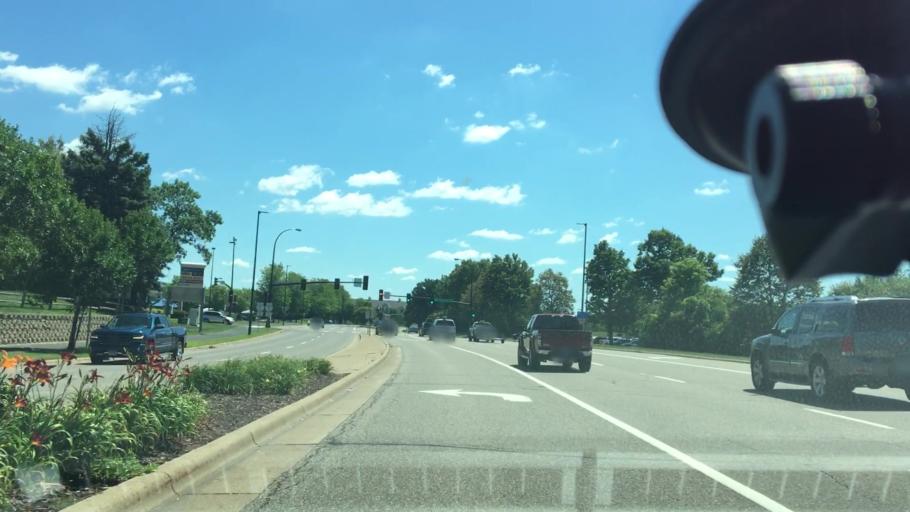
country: US
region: Minnesota
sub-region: Hennepin County
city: Maple Grove
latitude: 45.0658
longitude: -93.4454
